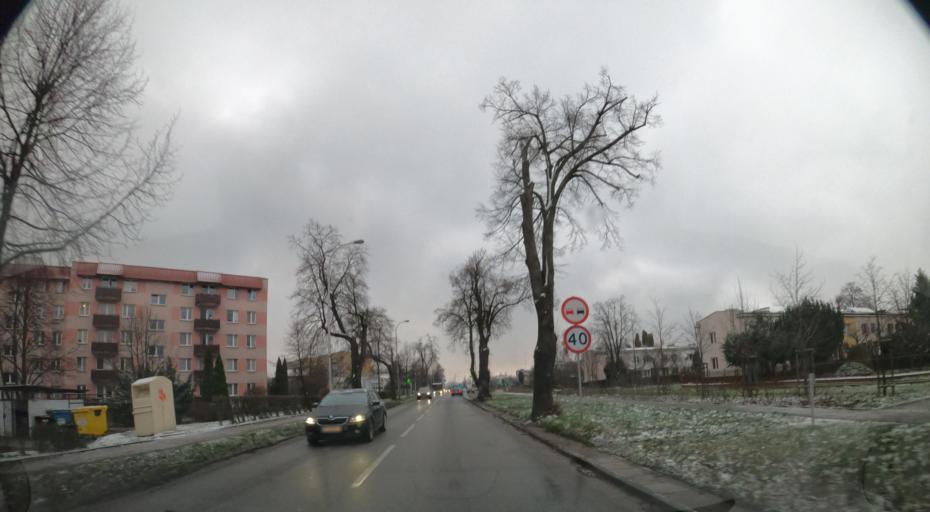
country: PL
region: Masovian Voivodeship
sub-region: Plock
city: Plock
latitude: 52.5533
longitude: 19.6719
